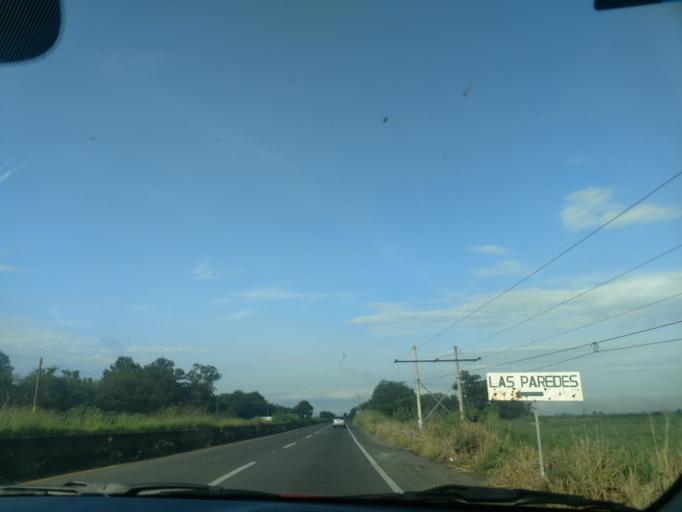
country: MX
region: Jalisco
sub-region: Ameca
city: Los Pocitos
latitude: 20.5513
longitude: -103.8971
